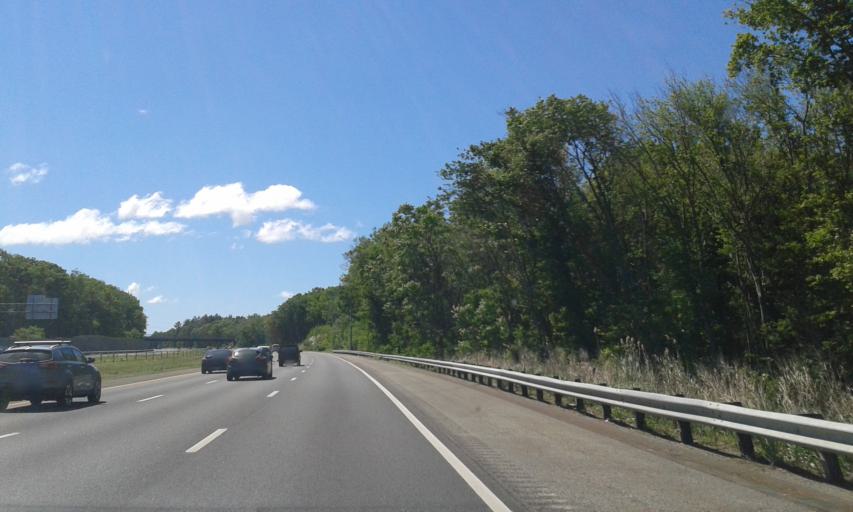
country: US
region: Massachusetts
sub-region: Middlesex County
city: Billerica
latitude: 42.5340
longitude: -71.2779
